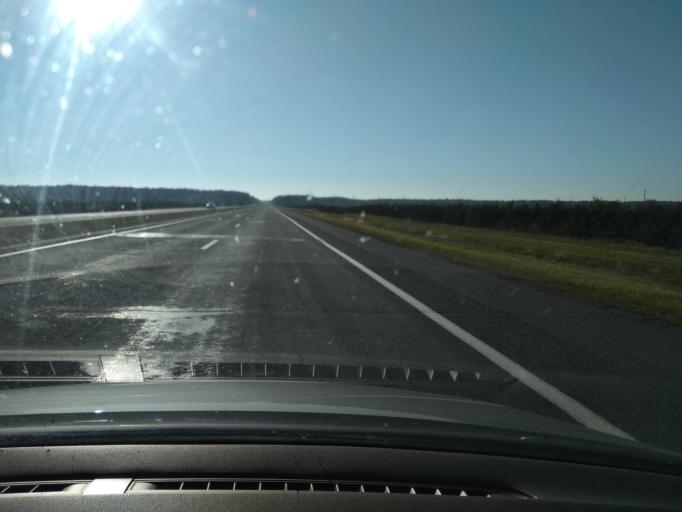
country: BY
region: Brest
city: Ivatsevichy
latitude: 52.6650
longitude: 25.2902
